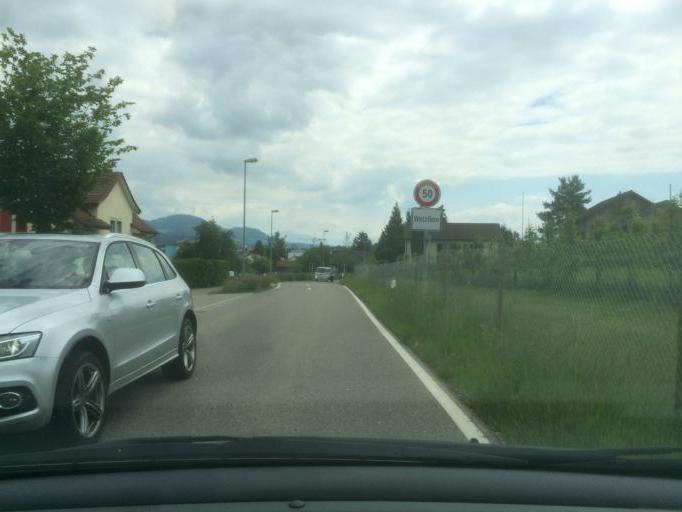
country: CH
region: Zurich
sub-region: Bezirk Hinwil
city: Wetzikon / Robenhausen
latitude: 47.3336
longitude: 8.7802
